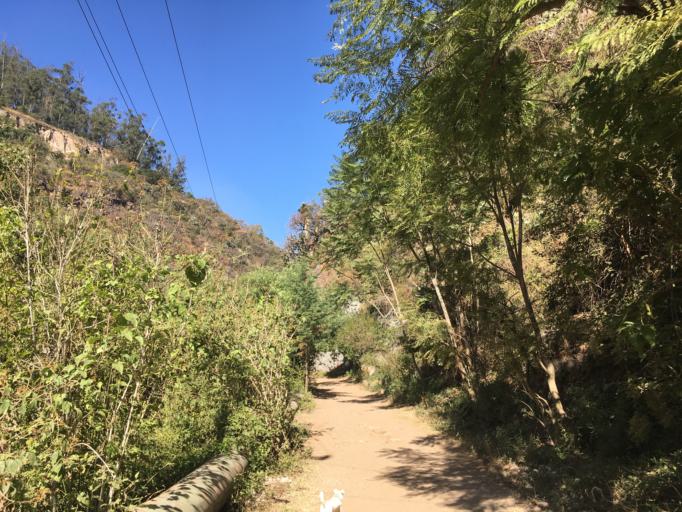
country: MX
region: Michoacan
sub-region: Morelia
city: Montana Monarca (Punta Altozano)
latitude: 19.6777
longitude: -101.1553
